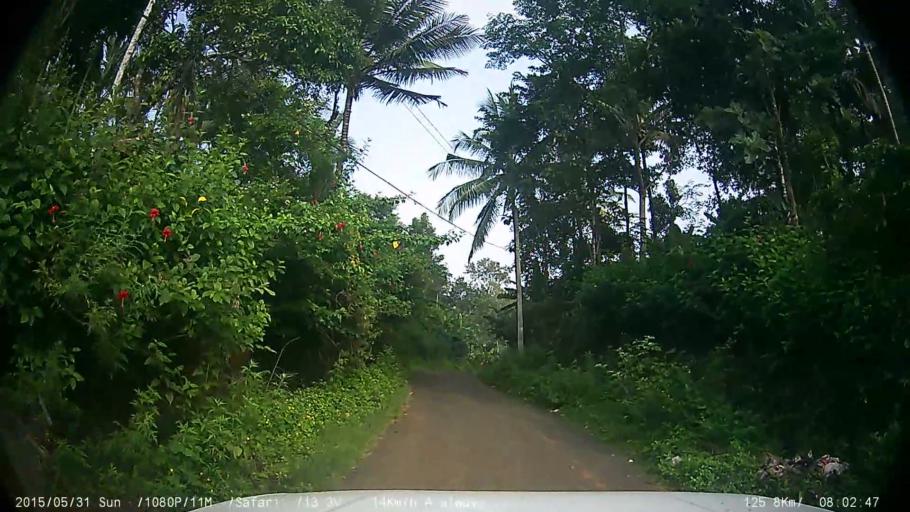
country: IN
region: Kerala
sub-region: Wayanad
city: Kalpetta
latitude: 11.6365
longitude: 76.0449
